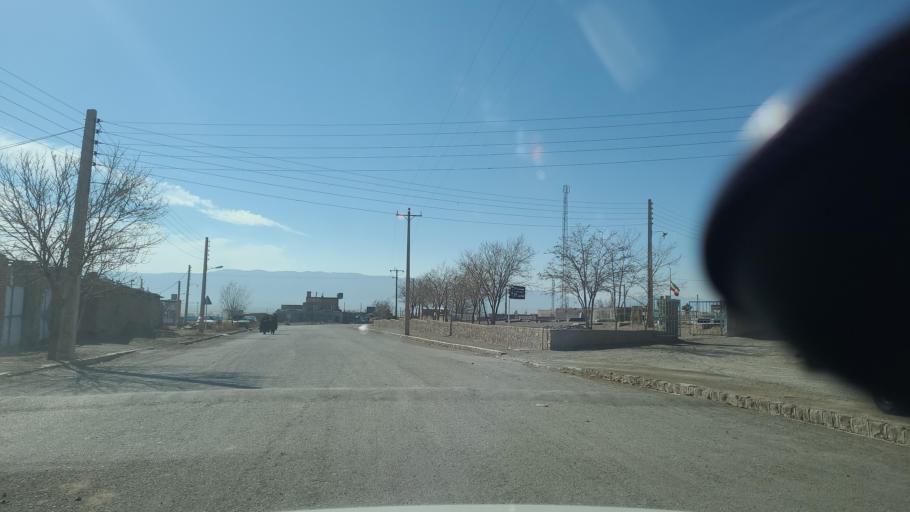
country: IR
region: Razavi Khorasan
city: Dowlatabad
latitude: 35.6221
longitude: 59.4789
